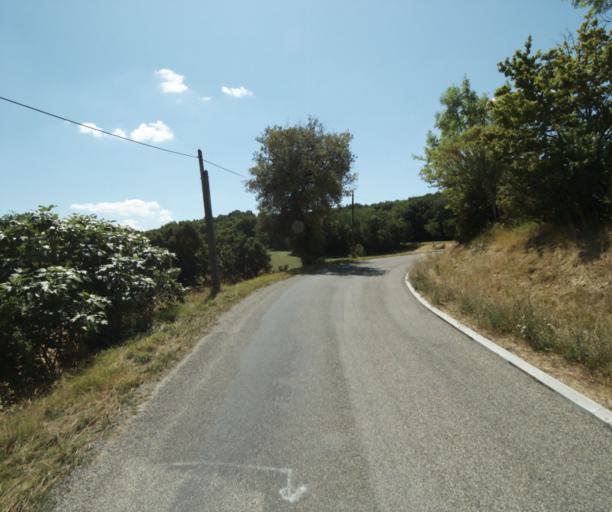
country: FR
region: Midi-Pyrenees
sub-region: Departement de la Haute-Garonne
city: Saint-Felix-Lauragais
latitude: 43.4824
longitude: 1.8713
